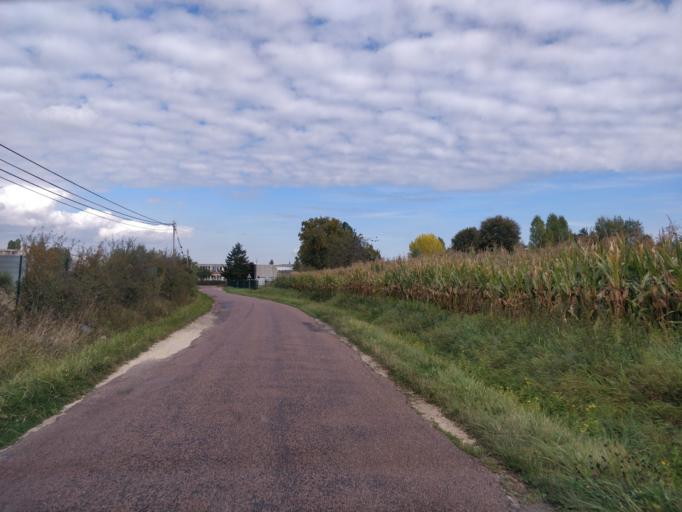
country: FR
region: Bourgogne
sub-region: Departement de l'Yonne
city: Saint-Florentin
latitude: 47.9955
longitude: 3.7163
